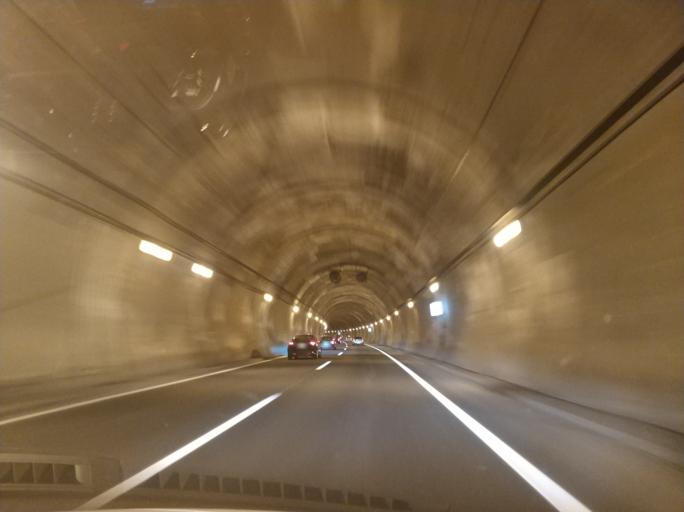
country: ES
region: Castille and Leon
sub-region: Provincia de Leon
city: Sena de Luna
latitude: 42.9167
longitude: -5.8900
